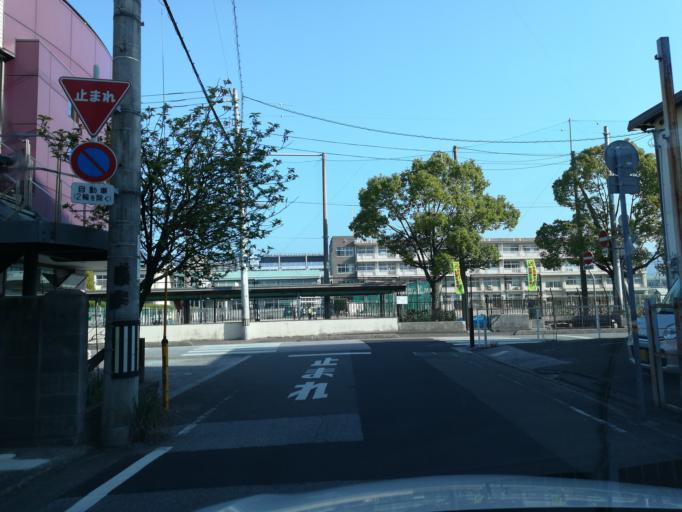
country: JP
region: Kochi
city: Kochi-shi
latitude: 33.5663
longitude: 133.5534
